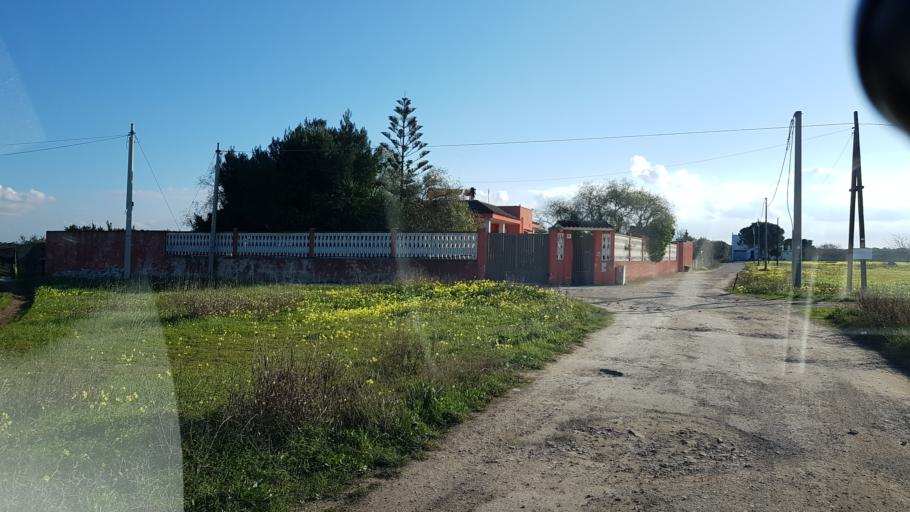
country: IT
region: Apulia
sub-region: Provincia di Brindisi
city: Tuturano
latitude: 40.5443
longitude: 17.9567
